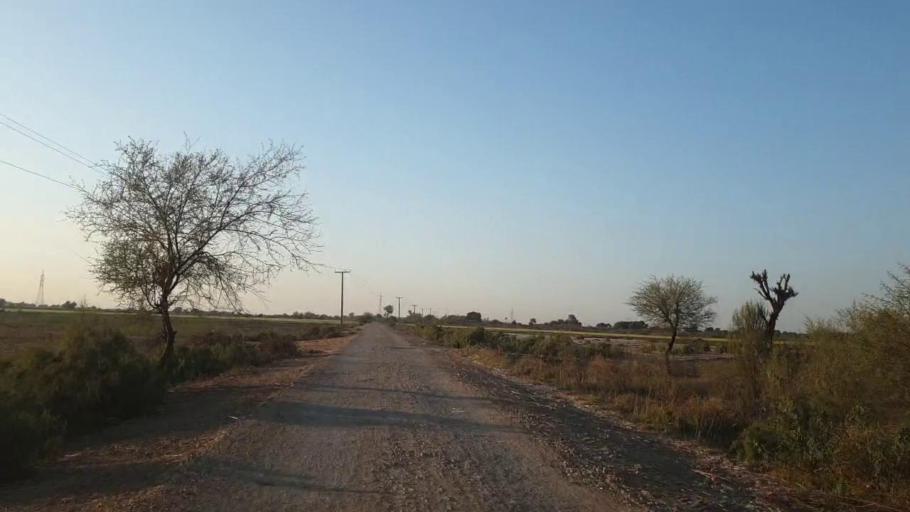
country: PK
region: Sindh
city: Mirpur Khas
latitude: 25.6985
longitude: 69.0458
